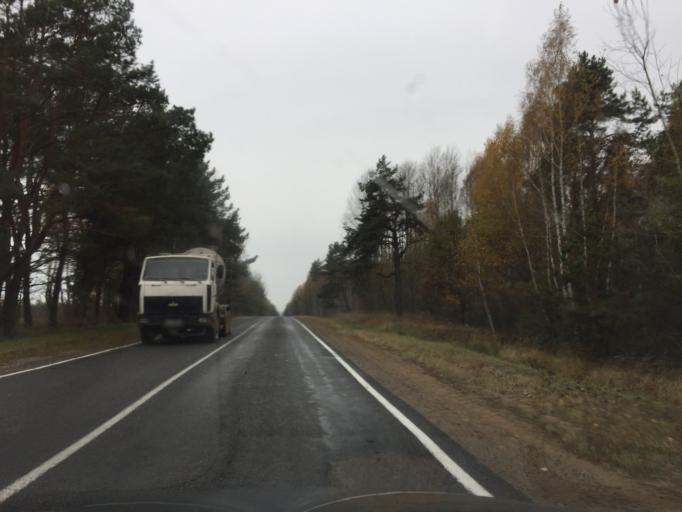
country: BY
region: Gomel
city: Karma
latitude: 53.3268
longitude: 30.7747
